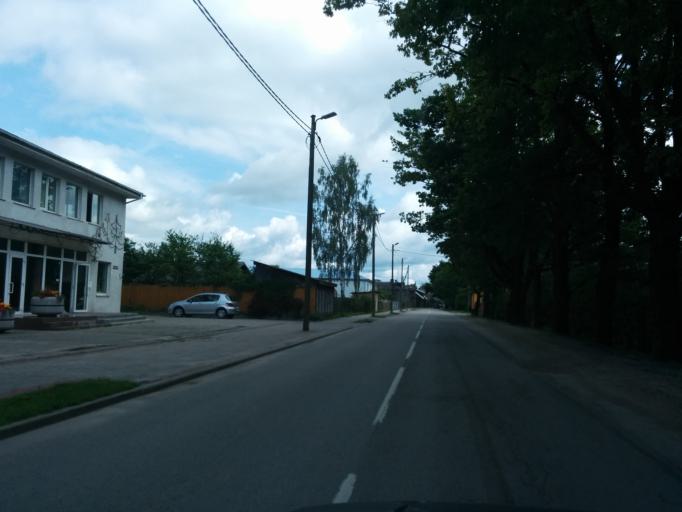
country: LV
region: Jelgava
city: Jelgava
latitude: 56.6559
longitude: 23.7128
